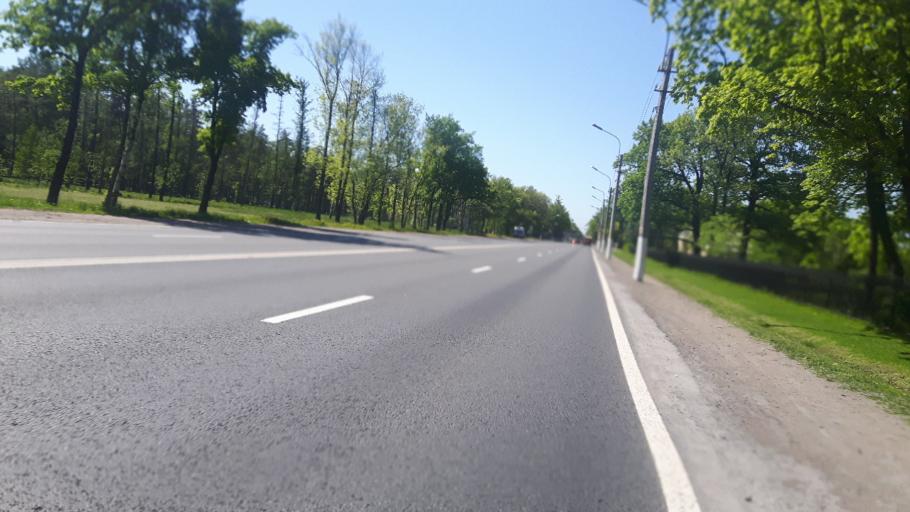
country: RU
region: St.-Petersburg
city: Peterhof
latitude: 59.8766
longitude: 29.9332
